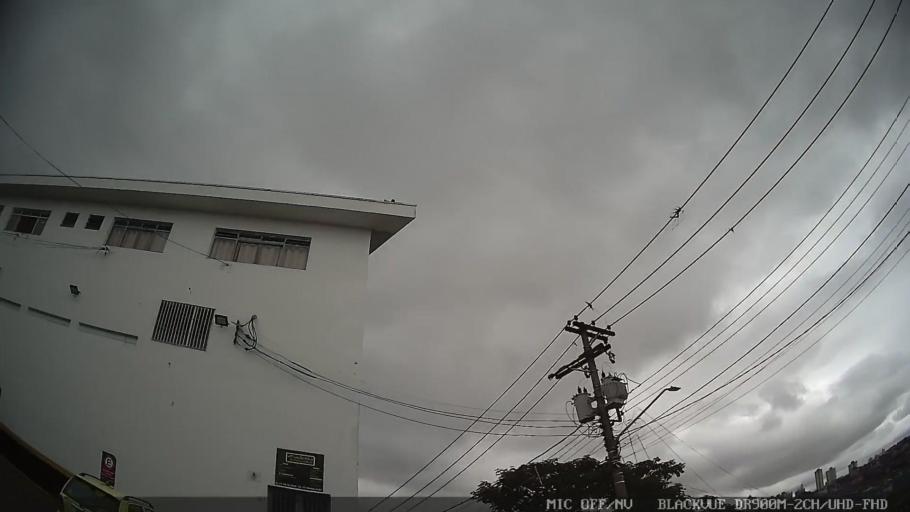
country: BR
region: Sao Paulo
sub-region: Osasco
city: Osasco
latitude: -23.4798
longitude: -46.7126
